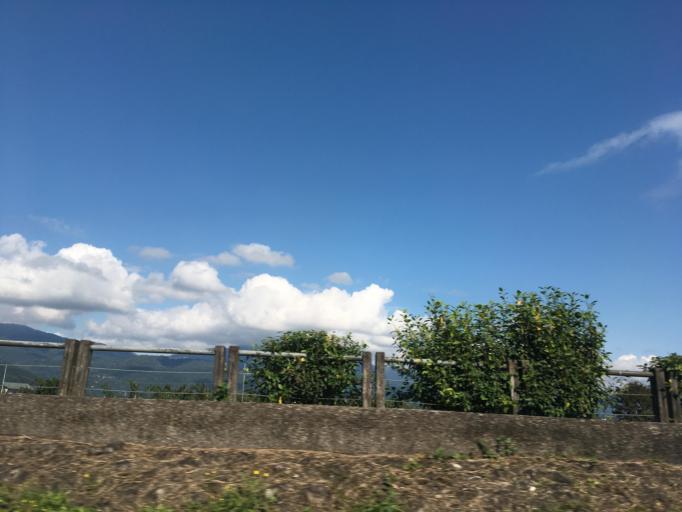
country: TW
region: Taiwan
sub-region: Yilan
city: Yilan
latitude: 24.7506
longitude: 121.7245
